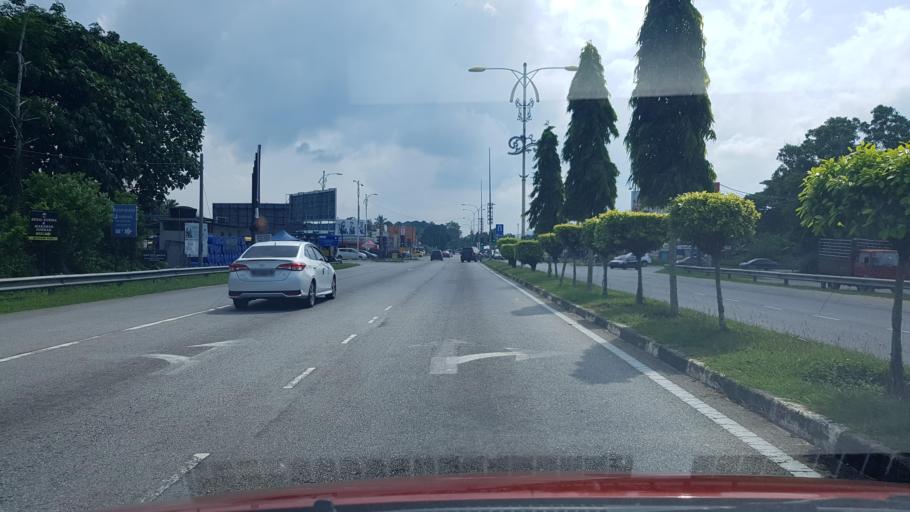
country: MY
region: Terengganu
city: Kuala Terengganu
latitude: 5.3395
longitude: 103.1027
